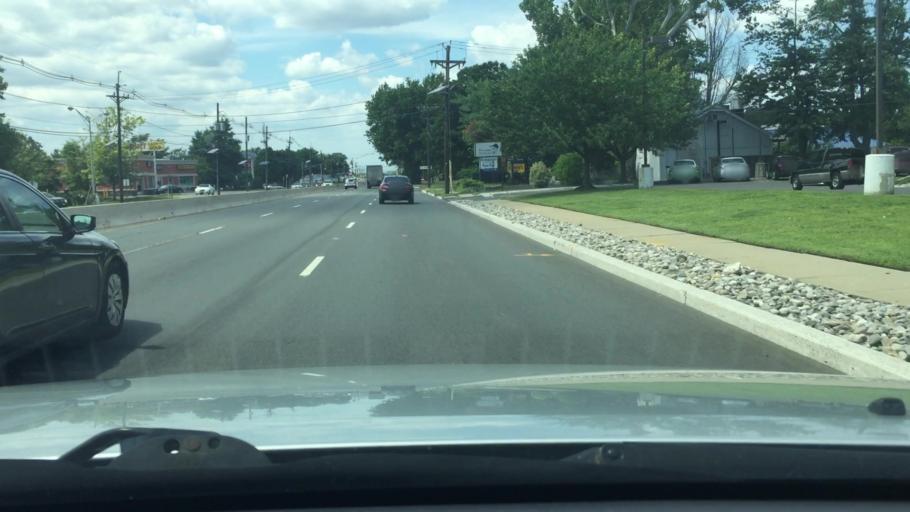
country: US
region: New Jersey
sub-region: Middlesex County
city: Old Bridge
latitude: 40.4232
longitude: -74.3784
